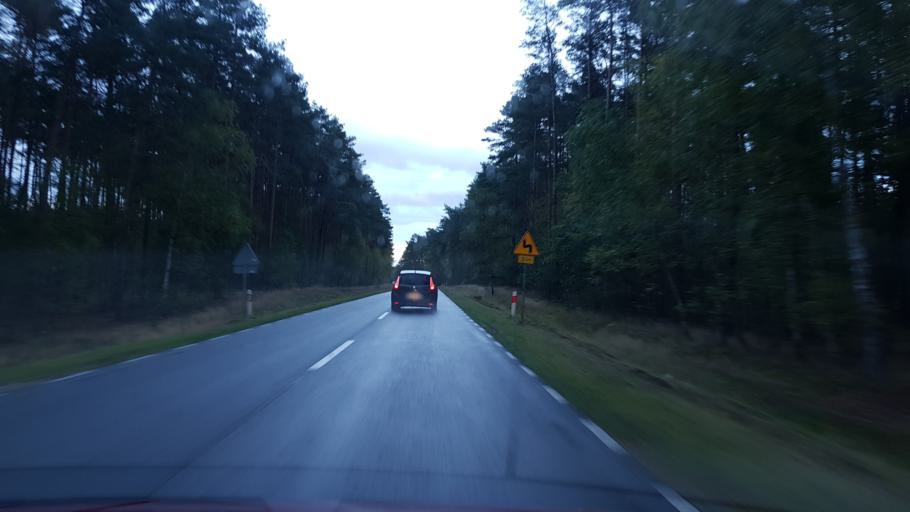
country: PL
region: Greater Poland Voivodeship
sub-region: Powiat pilski
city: Pila
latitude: 53.1924
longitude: 16.8206
